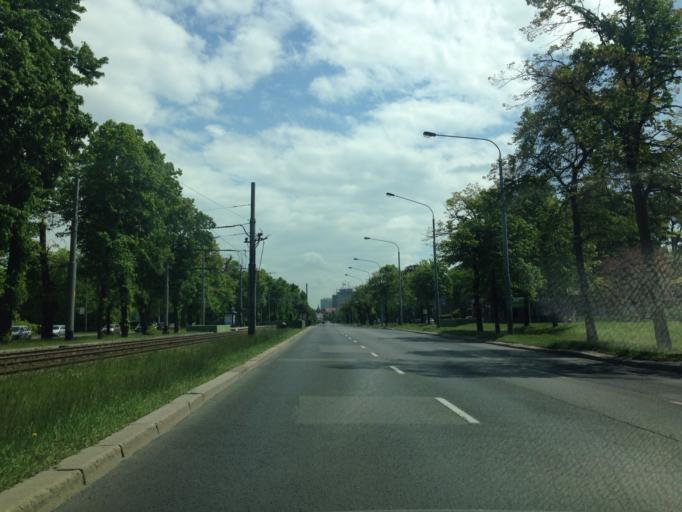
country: PL
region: Pomeranian Voivodeship
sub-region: Gdansk
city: Gdansk
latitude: 54.3675
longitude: 18.6324
